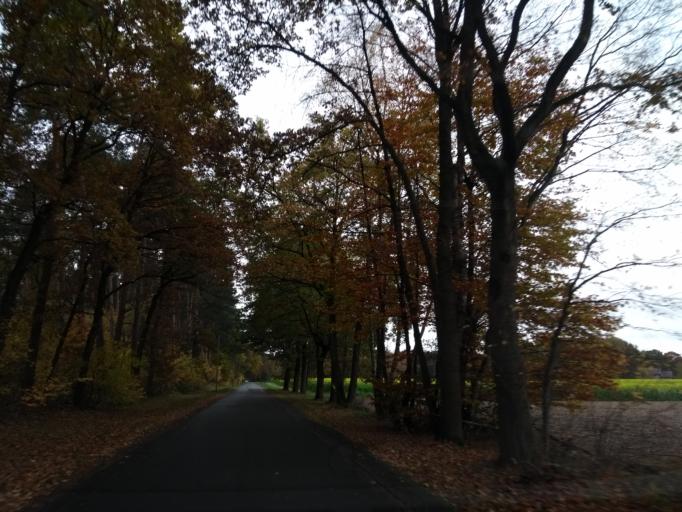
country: DE
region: North Rhine-Westphalia
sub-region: Regierungsbezirk Detmold
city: Hovelhof
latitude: 51.7780
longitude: 8.6849
